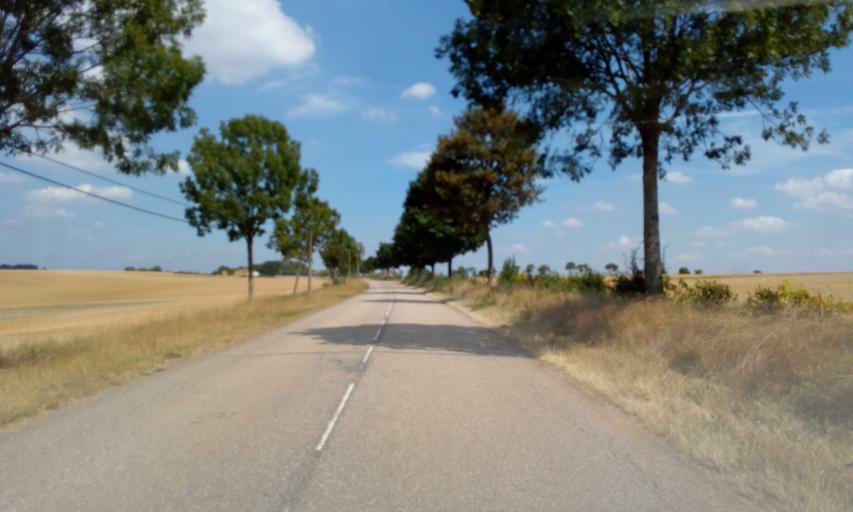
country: FR
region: Lorraine
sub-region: Departement de Meurthe-et-Moselle
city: Montauville
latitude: 48.9364
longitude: 5.9147
